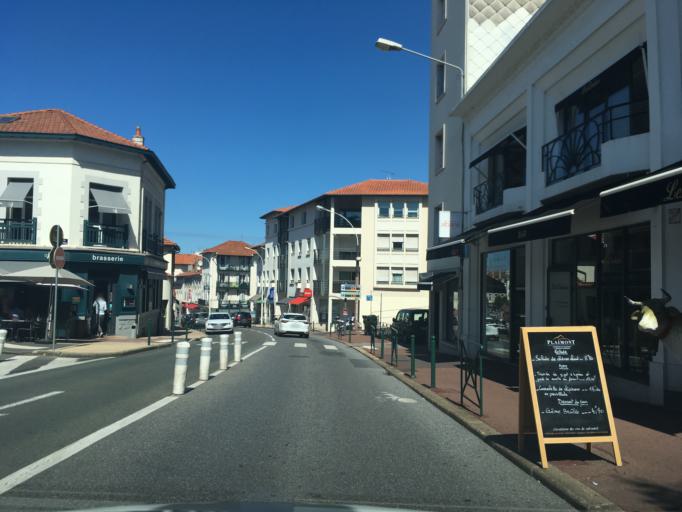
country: FR
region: Aquitaine
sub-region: Departement des Pyrenees-Atlantiques
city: Biarritz
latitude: 43.4798
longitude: -1.5586
